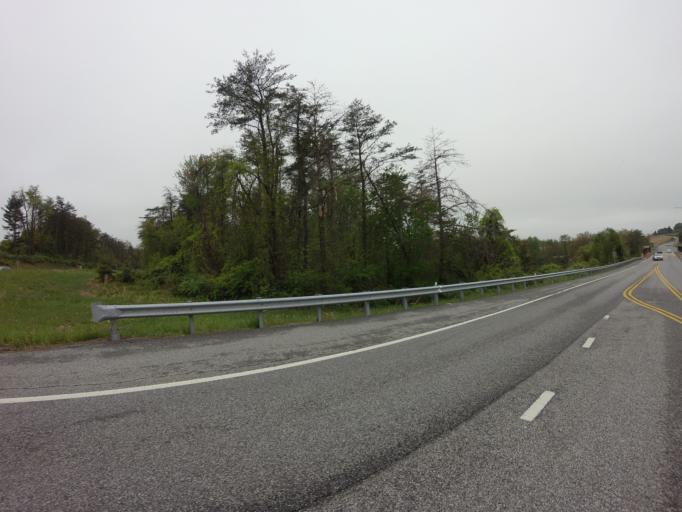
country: US
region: Maryland
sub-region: Baltimore County
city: Hunt Valley
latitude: 39.5915
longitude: -76.6718
